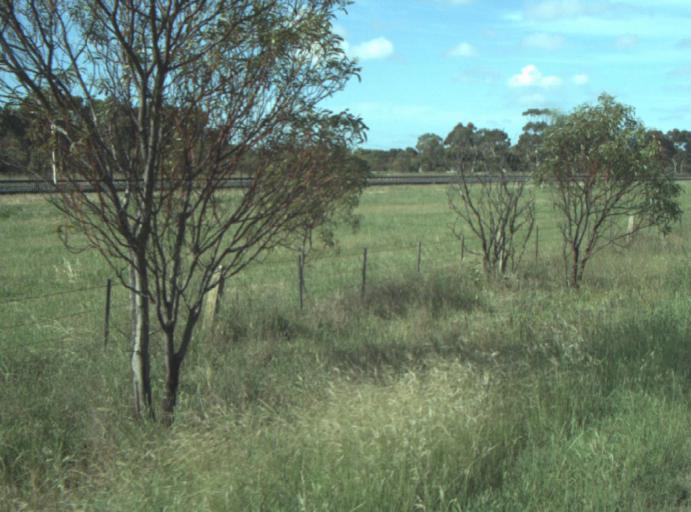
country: AU
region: Victoria
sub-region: Greater Geelong
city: Lara
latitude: -38.0124
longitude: 144.4255
